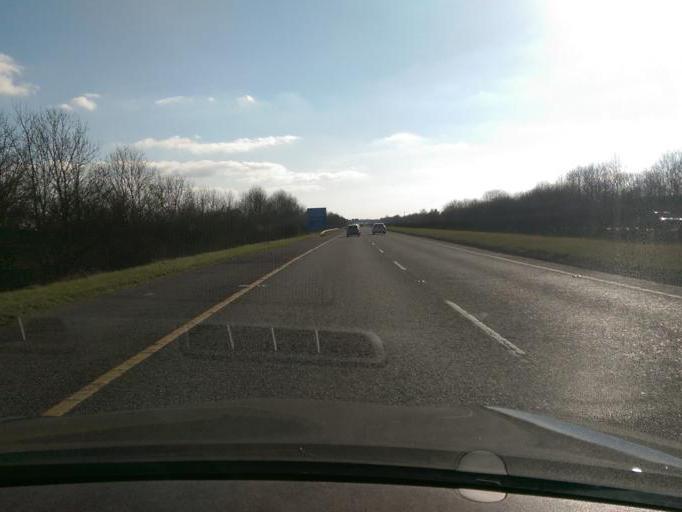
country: IE
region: Leinster
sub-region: Kildare
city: Naas
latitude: 53.1936
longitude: -6.7239
